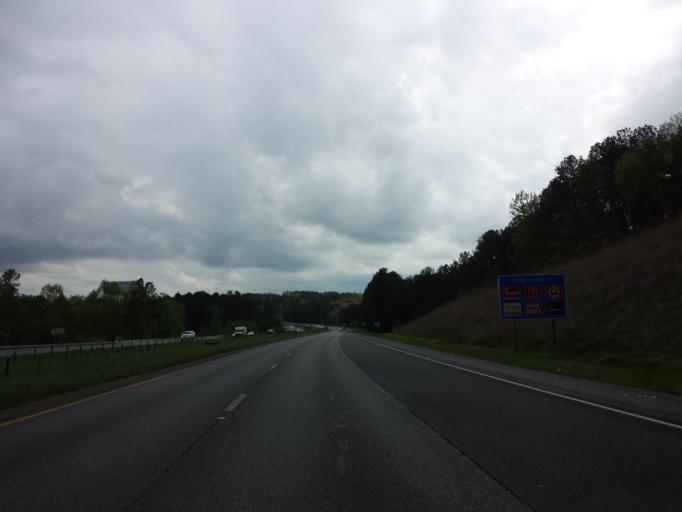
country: US
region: Georgia
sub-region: Cherokee County
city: Woodstock
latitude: 34.1385
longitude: -84.5213
